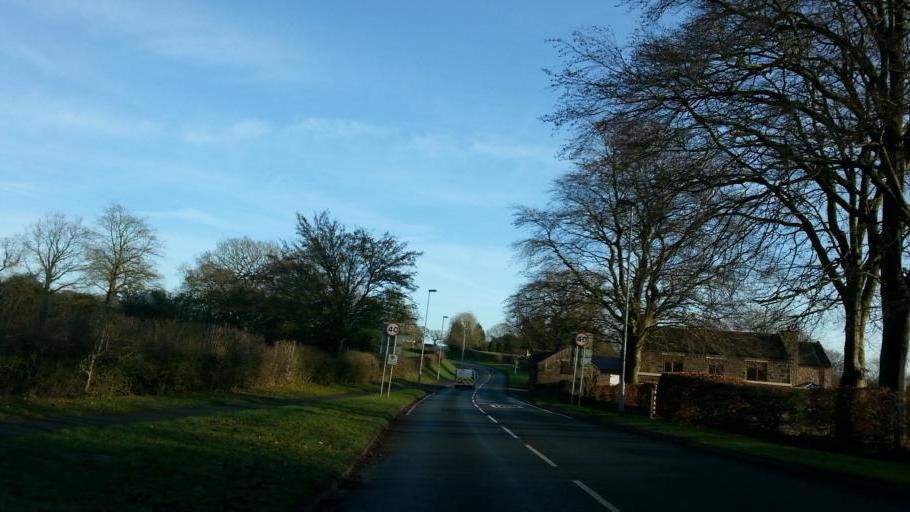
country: GB
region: England
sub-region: Staffordshire
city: Biddulph
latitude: 53.0762
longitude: -2.1321
